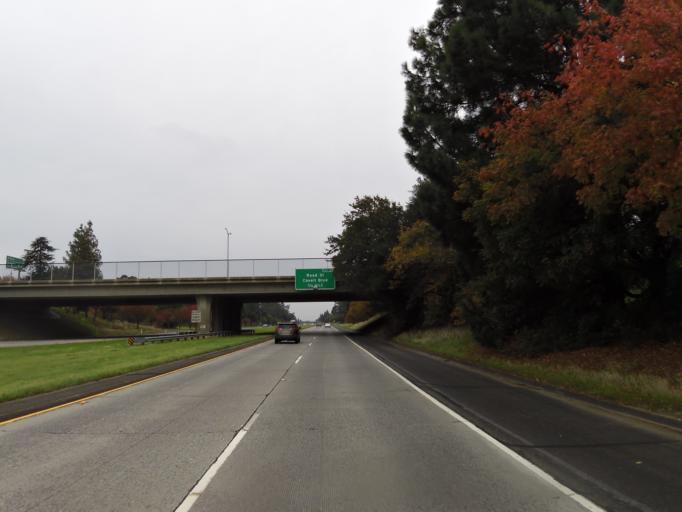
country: US
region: California
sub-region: Yolo County
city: Davis
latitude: 38.5456
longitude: -121.7680
